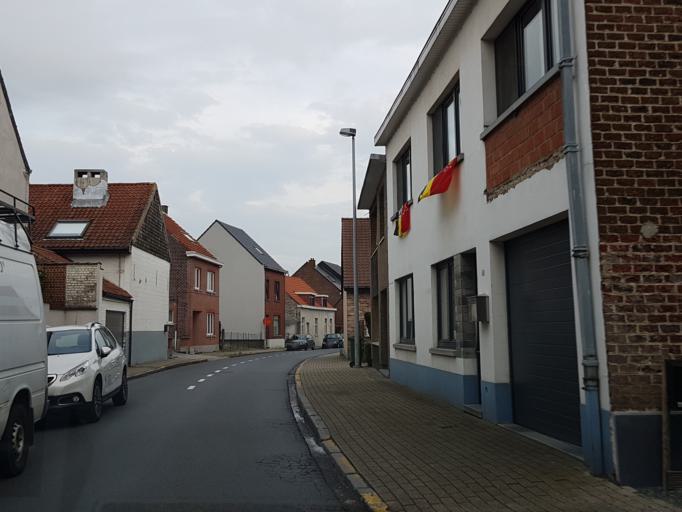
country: BE
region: Flanders
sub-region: Provincie Oost-Vlaanderen
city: Denderleeuw
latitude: 50.8940
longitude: 4.0926
